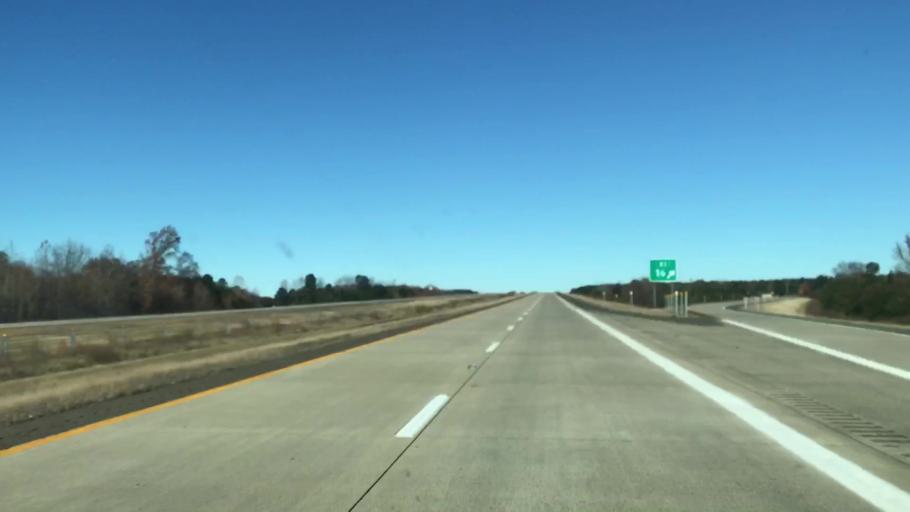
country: US
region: Texas
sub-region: Bowie County
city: Texarkana
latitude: 33.2471
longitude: -93.8807
